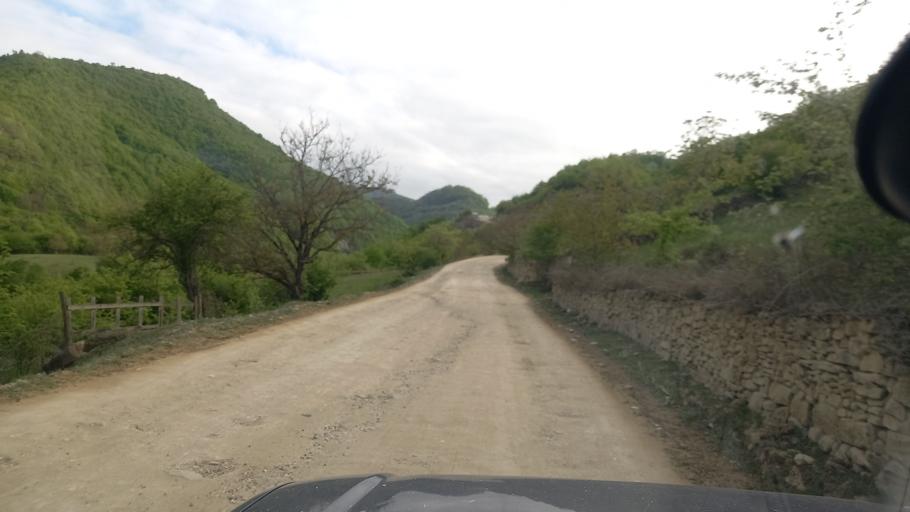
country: RU
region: Dagestan
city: Khuchni
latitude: 41.9693
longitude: 47.8766
